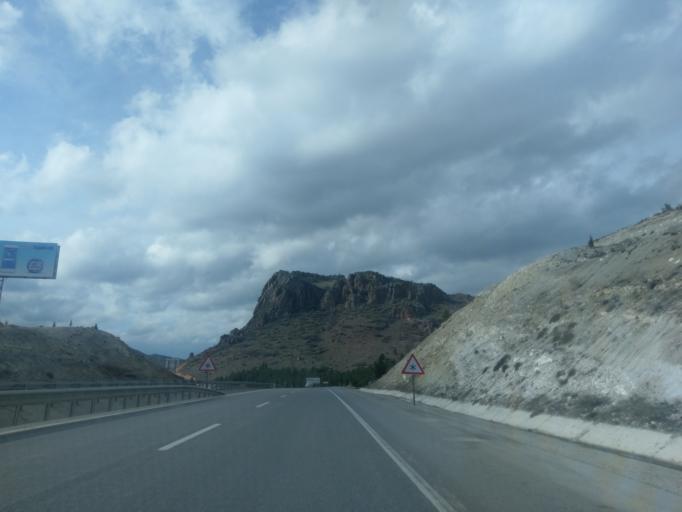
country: TR
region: Kuetahya
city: Sabuncu
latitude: 39.5723
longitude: 30.1038
